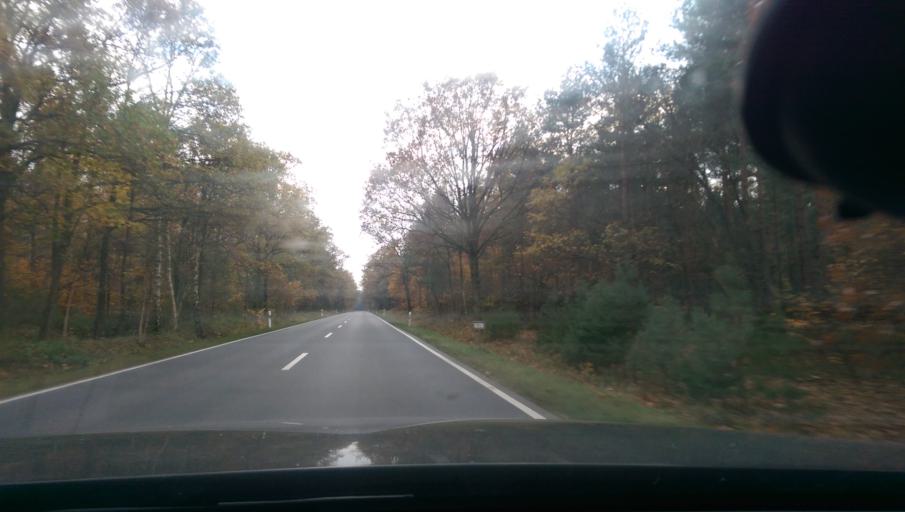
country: DE
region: Lower Saxony
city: Hambuhren
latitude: 52.6241
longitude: 9.9297
